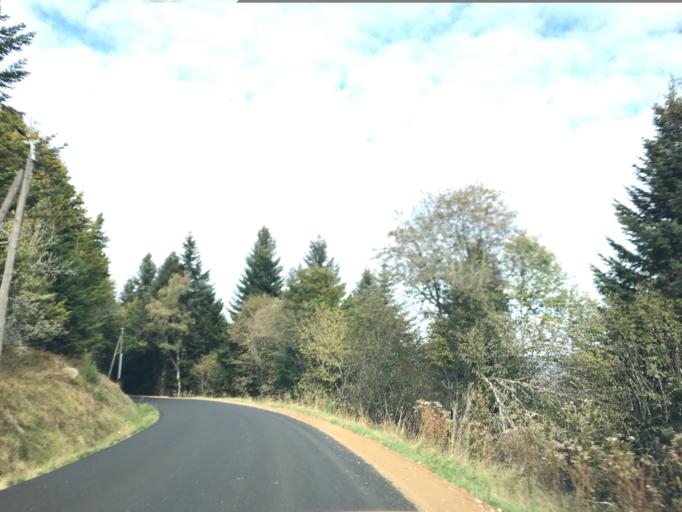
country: FR
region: Auvergne
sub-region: Departement du Puy-de-Dome
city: Celles-sur-Durolle
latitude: 45.8073
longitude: 3.6665
